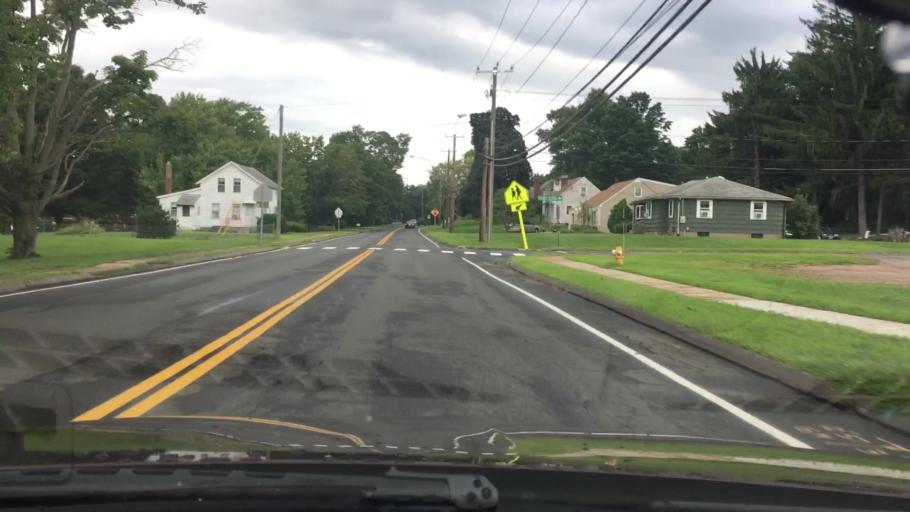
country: US
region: Connecticut
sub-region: Hartford County
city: Manchester
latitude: 41.7566
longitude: -72.5415
